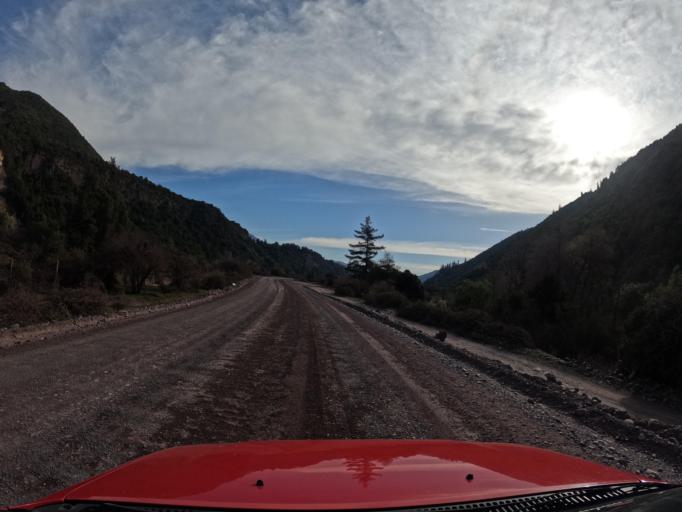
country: CL
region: O'Higgins
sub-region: Provincia de Colchagua
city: Chimbarongo
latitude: -34.9985
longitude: -70.7953
